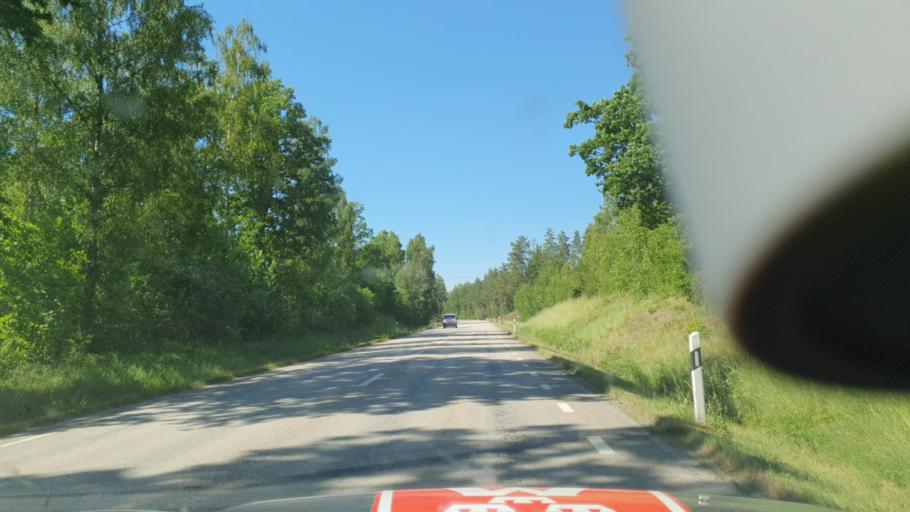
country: SE
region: Kalmar
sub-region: Emmaboda Kommun
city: Emmaboda
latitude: 56.5677
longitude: 15.5971
